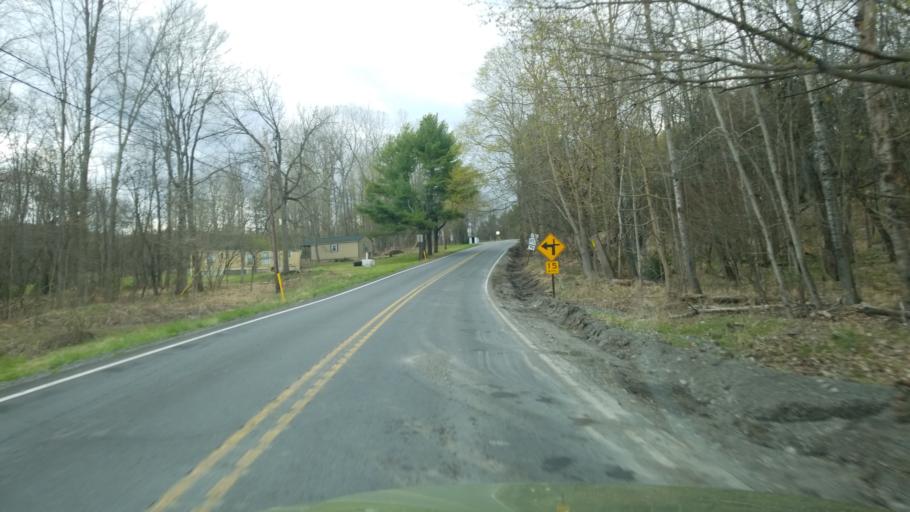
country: US
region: Pennsylvania
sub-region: Clearfield County
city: Curwensville
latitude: 40.8791
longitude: -78.4621
